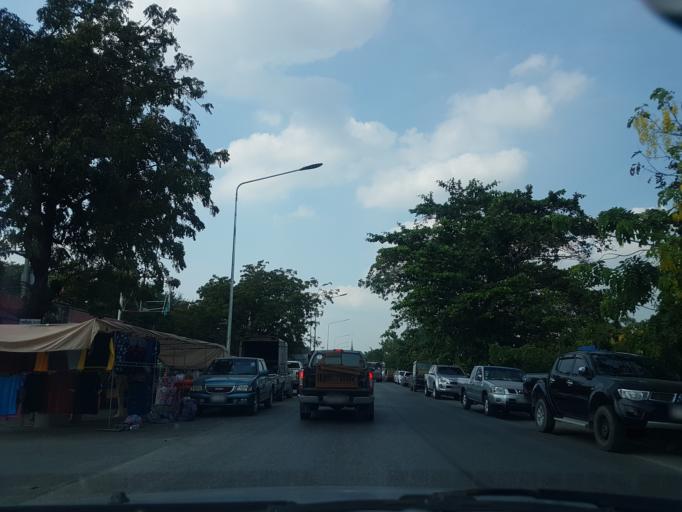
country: TH
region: Phra Nakhon Si Ayutthaya
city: Phachi
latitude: 14.3950
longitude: 100.7945
